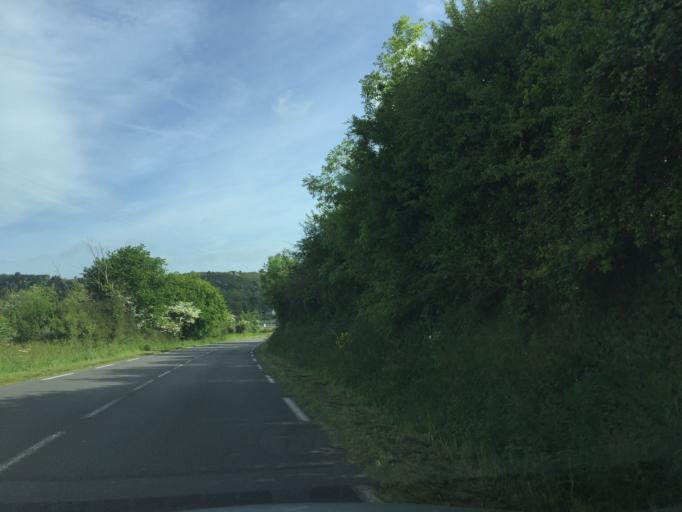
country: FR
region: Brittany
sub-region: Departement des Cotes-d'Armor
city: Matignon
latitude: 48.6155
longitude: -2.3380
